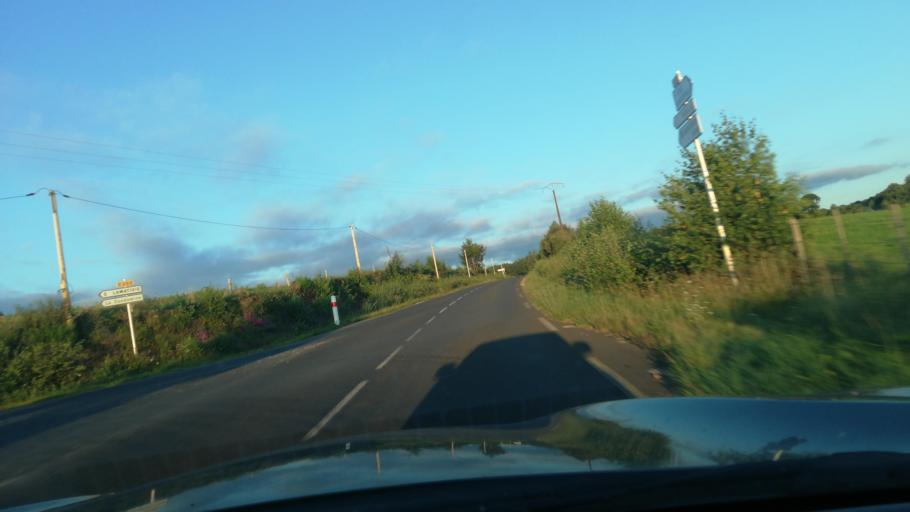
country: FR
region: Auvergne
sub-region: Departement du Cantal
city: Laroquebrou
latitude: 44.9498
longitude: 2.0985
